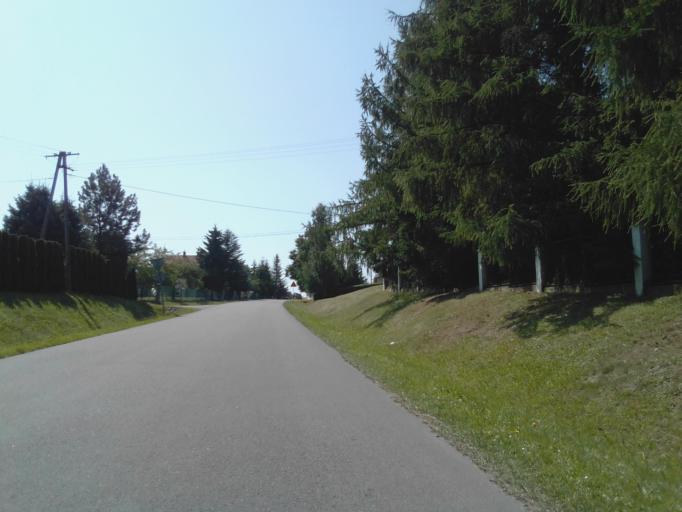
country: PL
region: Subcarpathian Voivodeship
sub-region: Powiat ropczycko-sedziszowski
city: Sedziszow Malopolski
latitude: 50.0666
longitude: 21.6631
